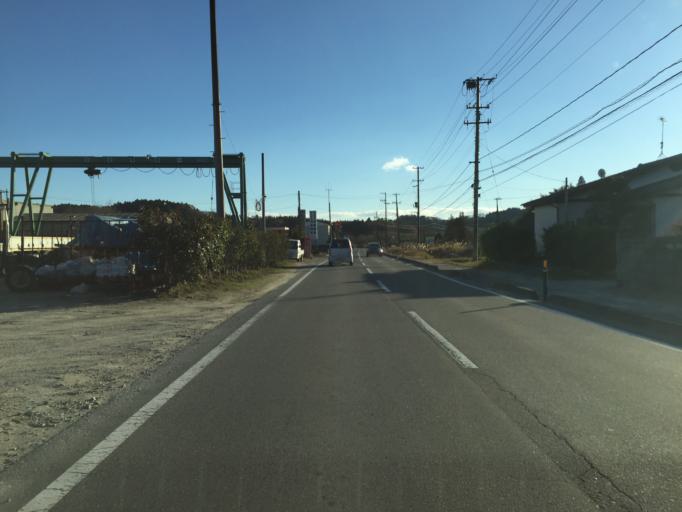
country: JP
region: Fukushima
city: Iwaki
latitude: 37.1052
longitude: 140.8624
